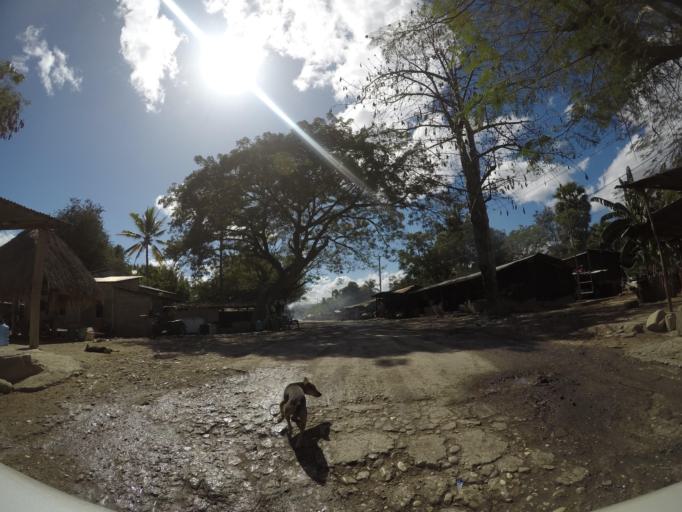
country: TL
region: Baucau
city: Baucau
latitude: -8.4853
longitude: 126.5612
